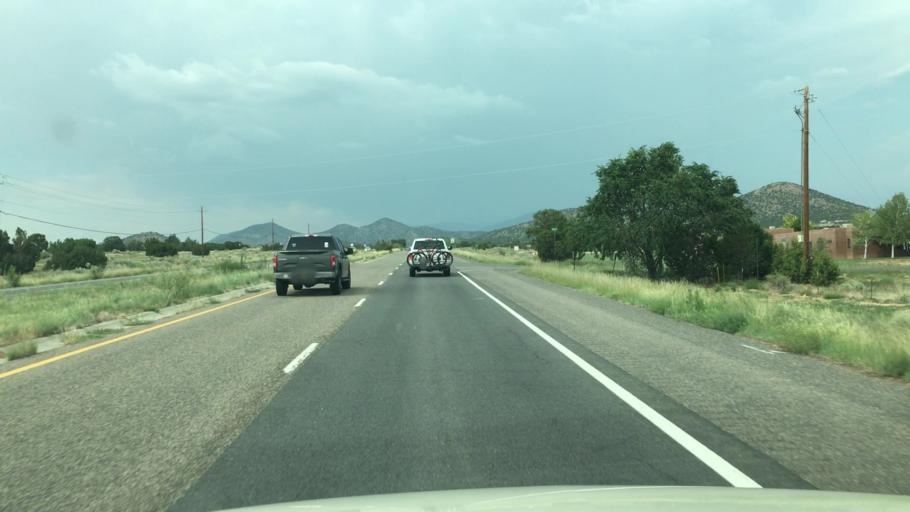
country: US
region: New Mexico
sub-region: Santa Fe County
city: Eldorado at Santa Fe
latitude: 35.5220
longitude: -105.8923
